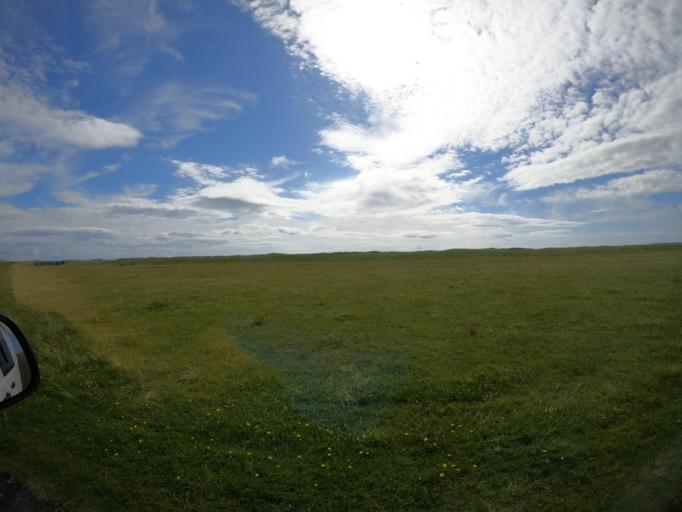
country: GB
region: Scotland
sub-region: Eilean Siar
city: Barra
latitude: 56.4928
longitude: -6.8671
